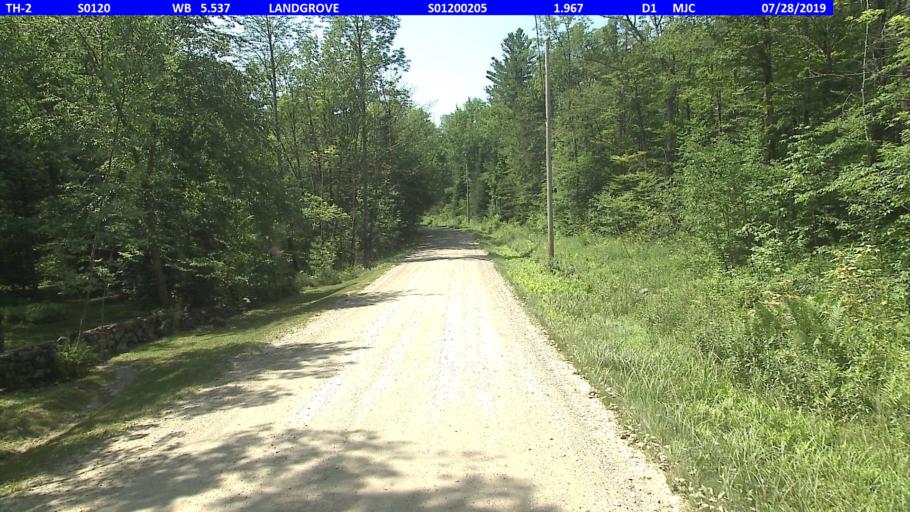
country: US
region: Vermont
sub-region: Bennington County
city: Manchester Center
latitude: 43.2864
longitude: -72.8537
